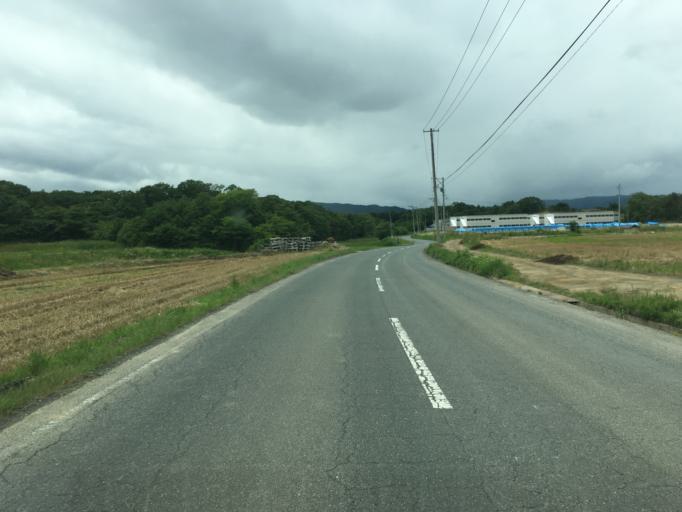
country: JP
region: Miyagi
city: Marumori
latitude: 37.7427
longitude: 140.9410
